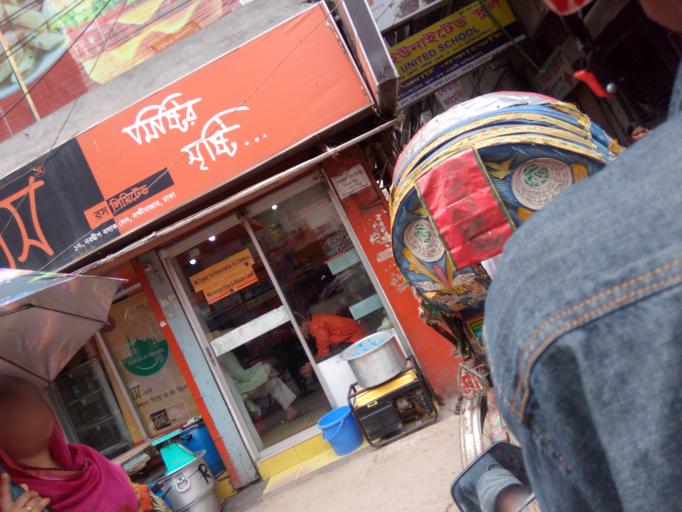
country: BD
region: Dhaka
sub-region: Dhaka
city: Dhaka
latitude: 23.7086
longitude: 90.4151
